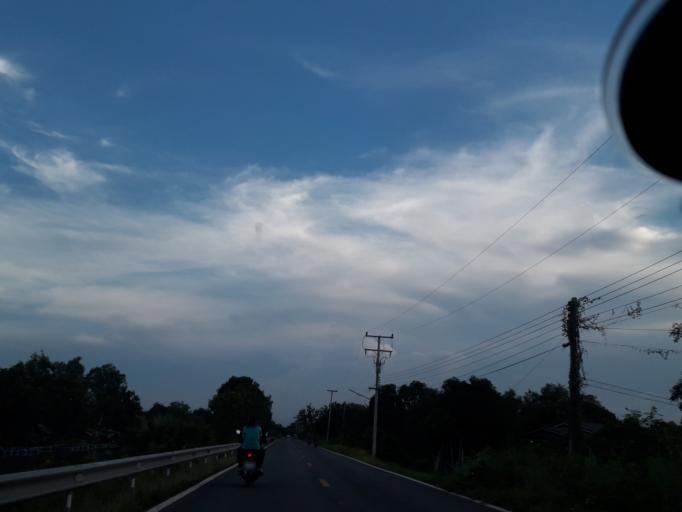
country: TH
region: Sara Buri
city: Nong Khae
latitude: 14.2822
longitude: 100.8912
